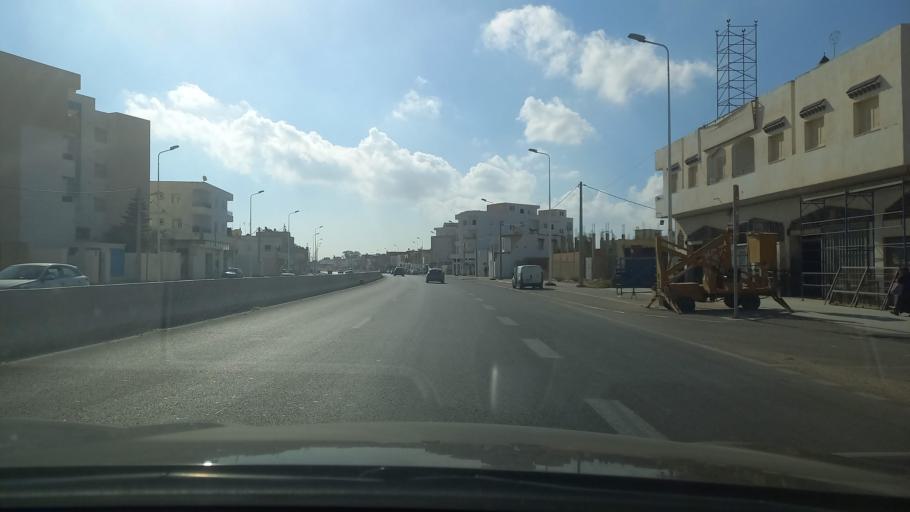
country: TN
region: Safaqis
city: Sfax
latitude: 34.7410
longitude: 10.7239
